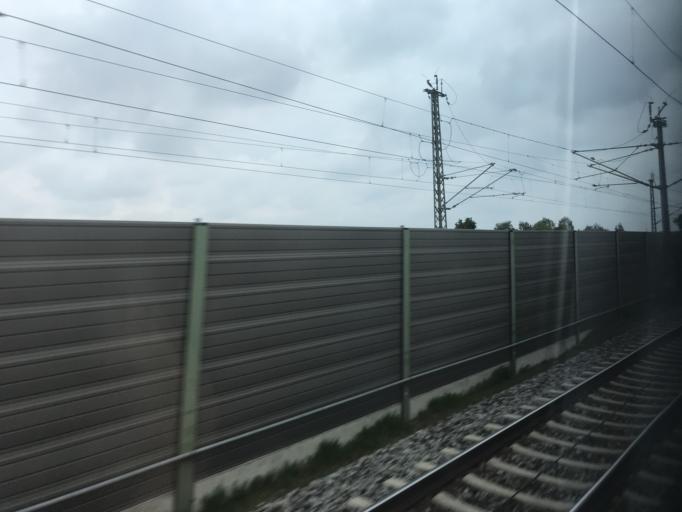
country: DE
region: Bavaria
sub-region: Swabia
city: Mering
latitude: 48.2656
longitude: 10.9828
